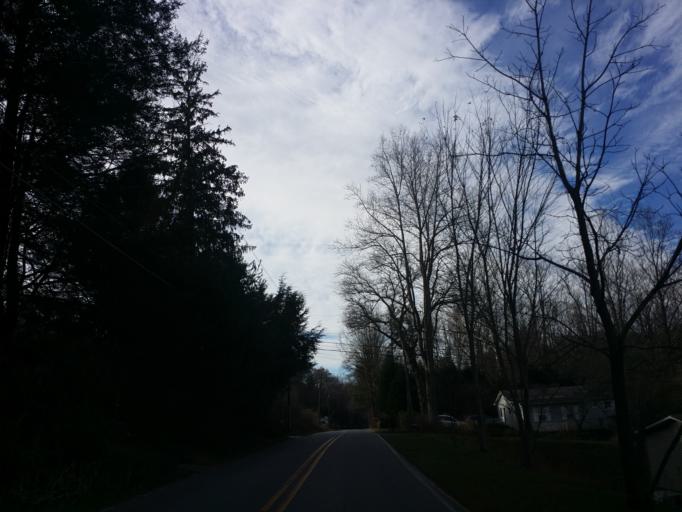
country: US
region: North Carolina
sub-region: Buncombe County
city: Swannanoa
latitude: 35.6295
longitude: -82.4267
